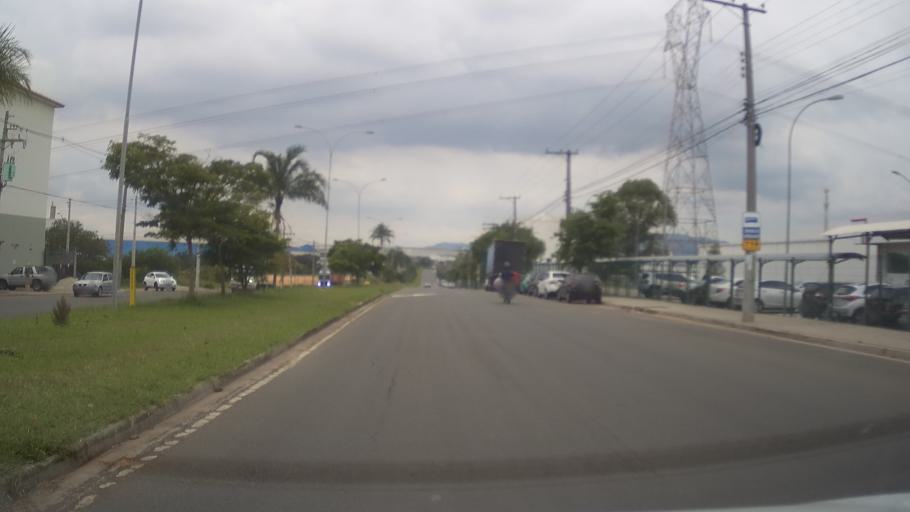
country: BR
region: Sao Paulo
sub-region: Itupeva
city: Itupeva
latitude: -23.1554
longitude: -47.0080
